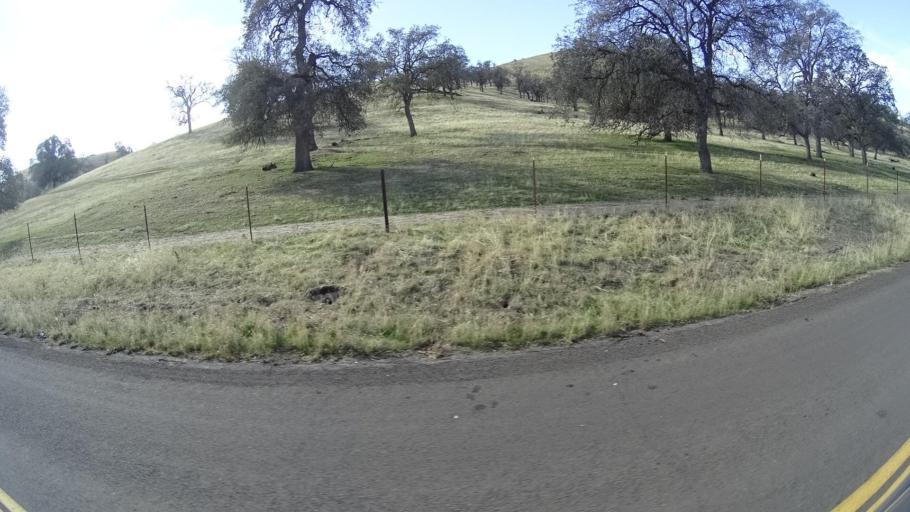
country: US
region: California
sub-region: Tulare County
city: Richgrove
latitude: 35.6673
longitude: -118.8483
